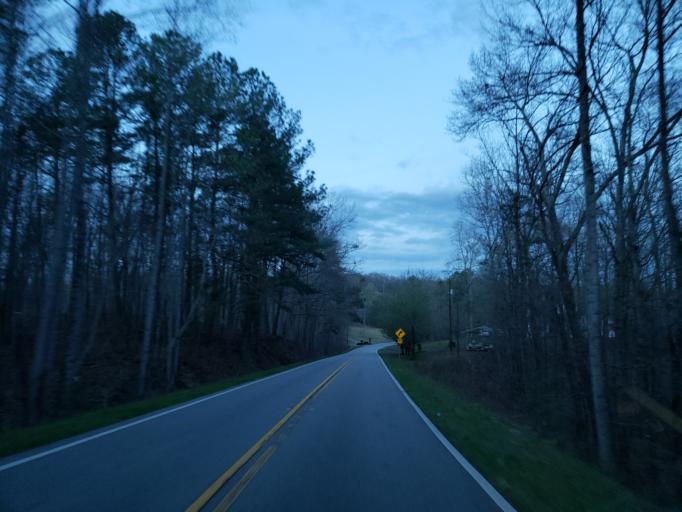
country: US
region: Georgia
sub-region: Paulding County
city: Dallas
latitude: 34.0062
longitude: -84.9116
